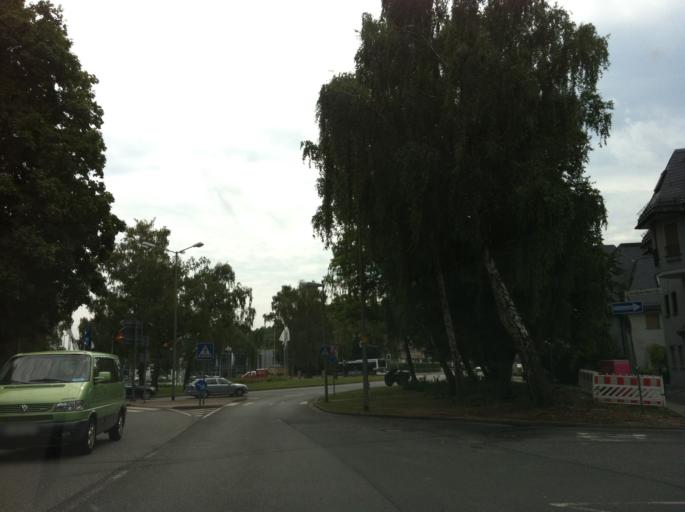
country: DE
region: Hesse
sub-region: Regierungsbezirk Darmstadt
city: Konigstein im Taunus
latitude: 50.1802
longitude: 8.4736
